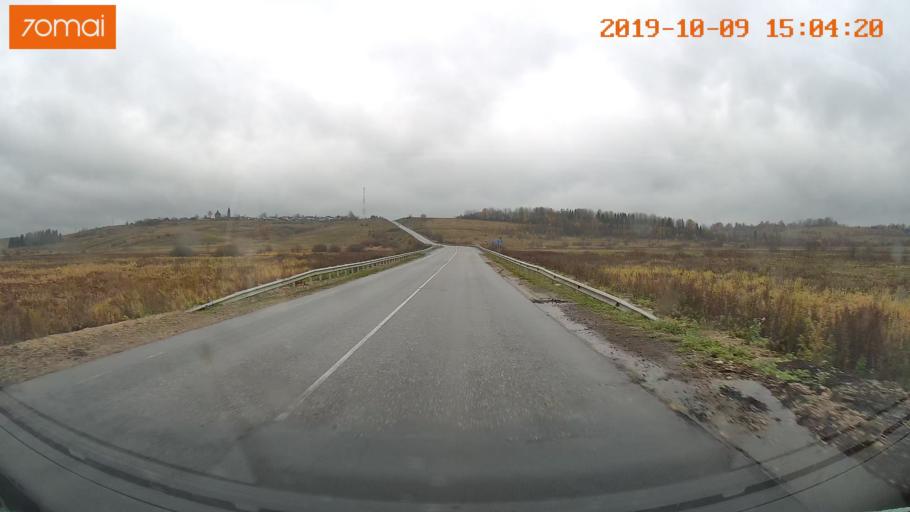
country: RU
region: Kostroma
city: Chistyye Bory
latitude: 58.2599
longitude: 41.6681
